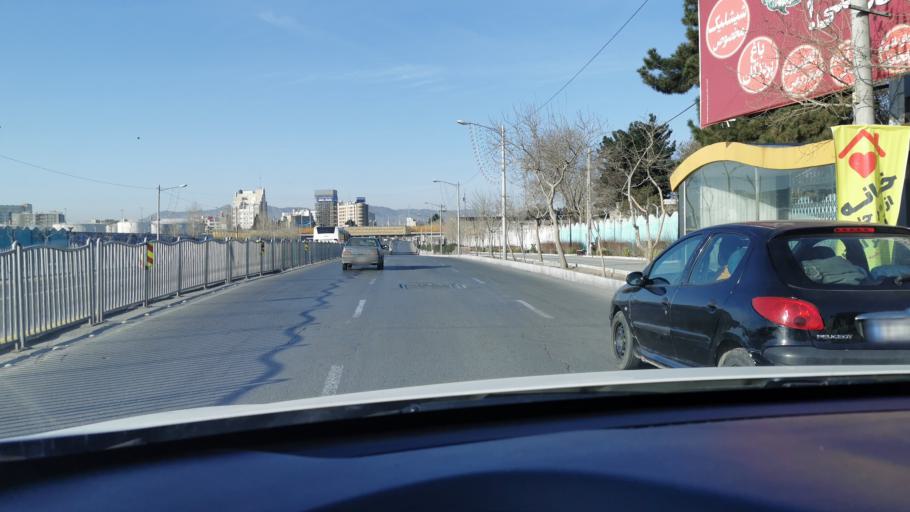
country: IR
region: Razavi Khorasan
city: Mashhad
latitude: 36.2987
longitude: 59.6326
